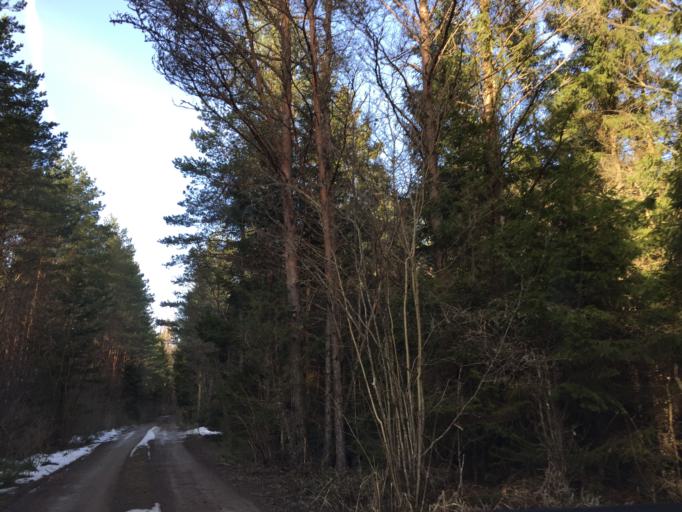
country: EE
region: Saare
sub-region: Kuressaare linn
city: Kuressaare
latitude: 58.3764
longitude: 22.0114
